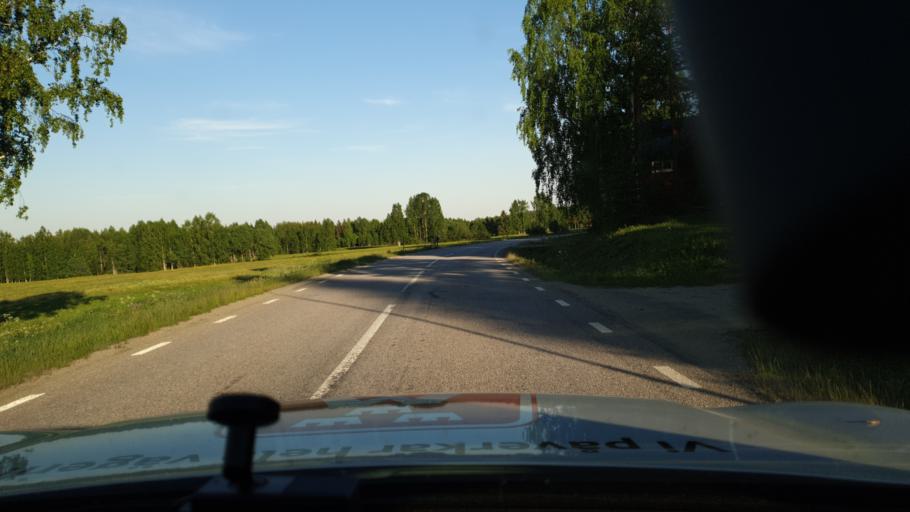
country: SE
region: Vaesterbotten
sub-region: Bjurholms Kommun
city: Bjurholm
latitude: 64.0342
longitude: 19.0588
